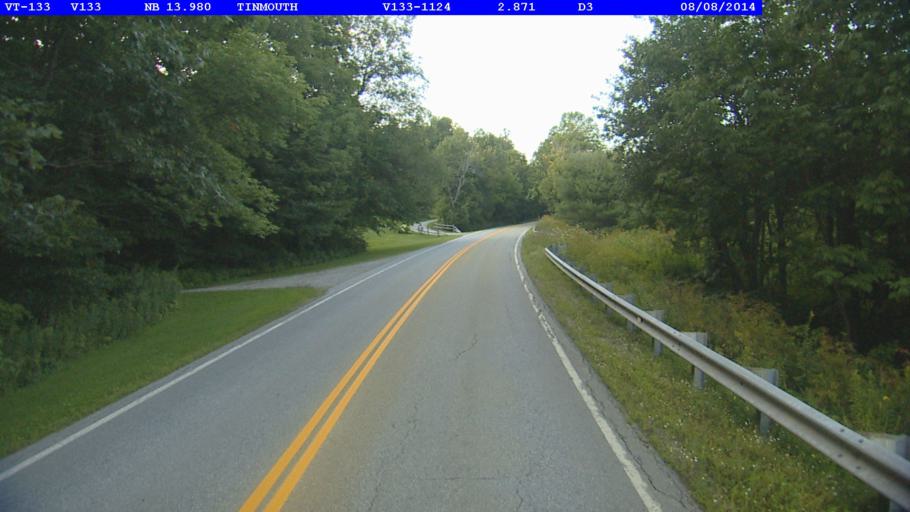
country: US
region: Vermont
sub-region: Rutland County
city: West Rutland
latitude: 43.4876
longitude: -73.0755
